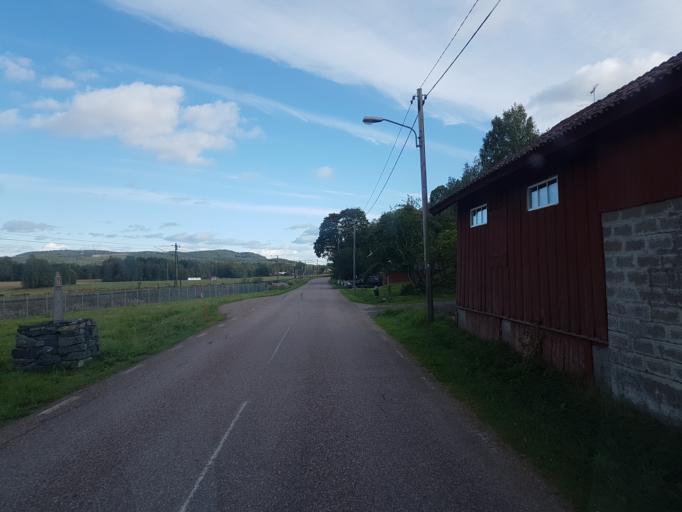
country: SE
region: Dalarna
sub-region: Saters Kommun
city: Saeter
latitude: 60.3591
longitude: 15.7414
